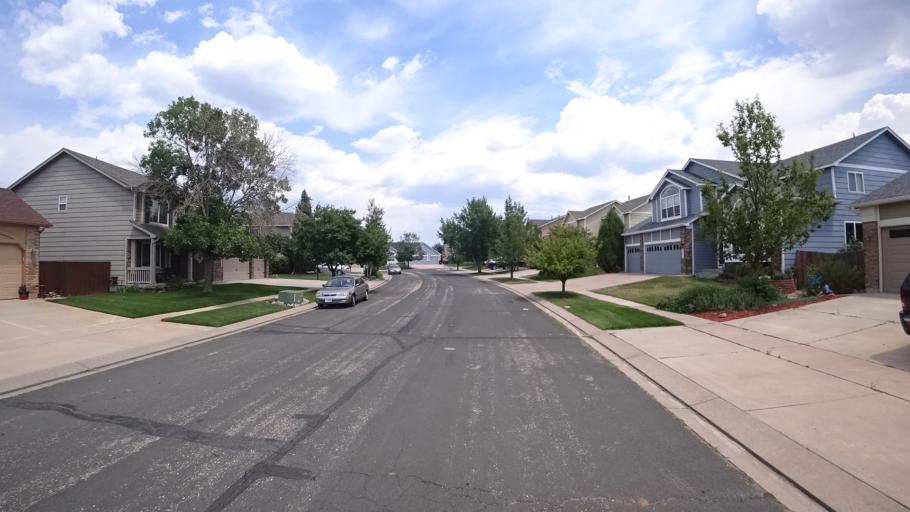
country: US
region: Colorado
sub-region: El Paso County
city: Black Forest
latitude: 38.9644
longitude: -104.7715
